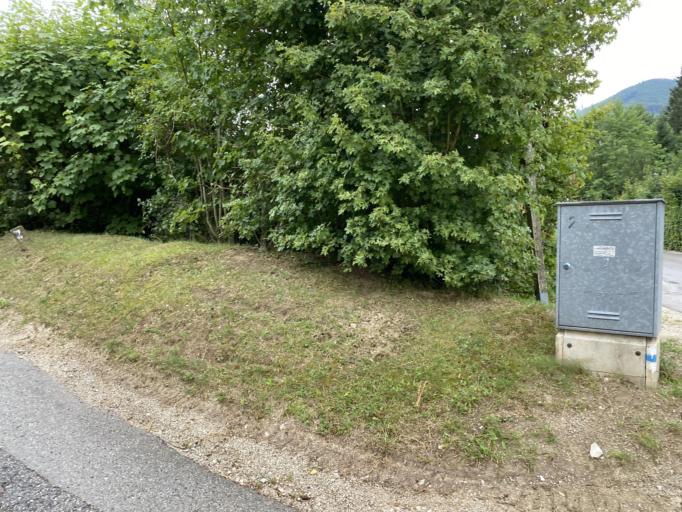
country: AT
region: Lower Austria
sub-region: Politischer Bezirk Baden
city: Altenmarkt an der Triesting
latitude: 48.0174
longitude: 15.9677
